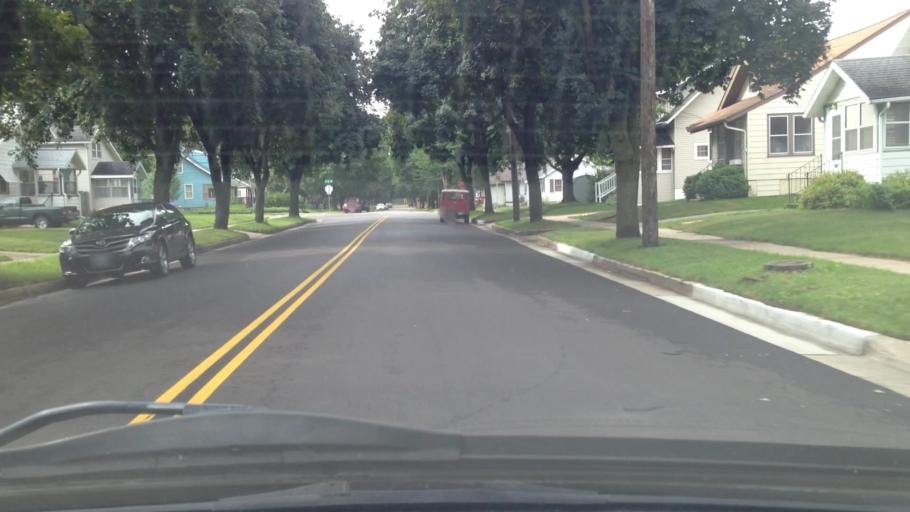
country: US
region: Minnesota
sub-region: Olmsted County
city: Rochester
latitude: 44.0178
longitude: -92.4488
